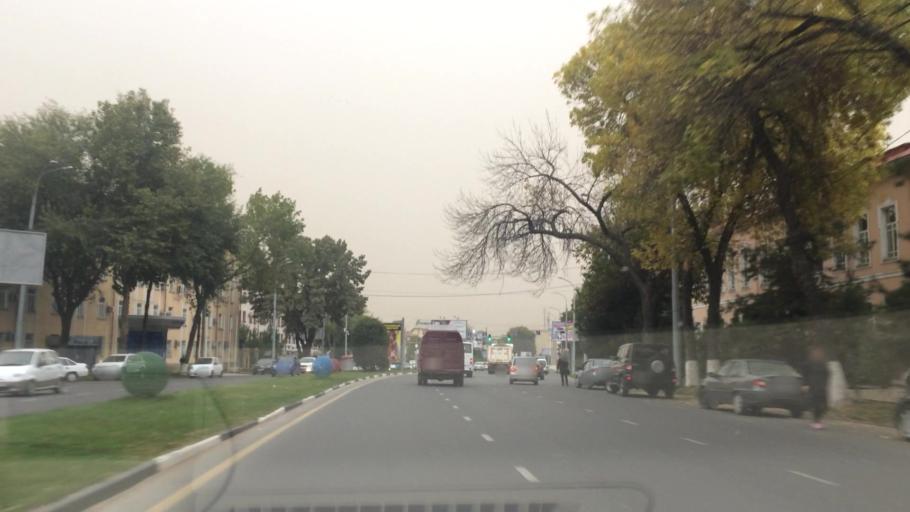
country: UZ
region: Toshkent Shahri
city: Tashkent
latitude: 41.3036
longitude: 69.2477
